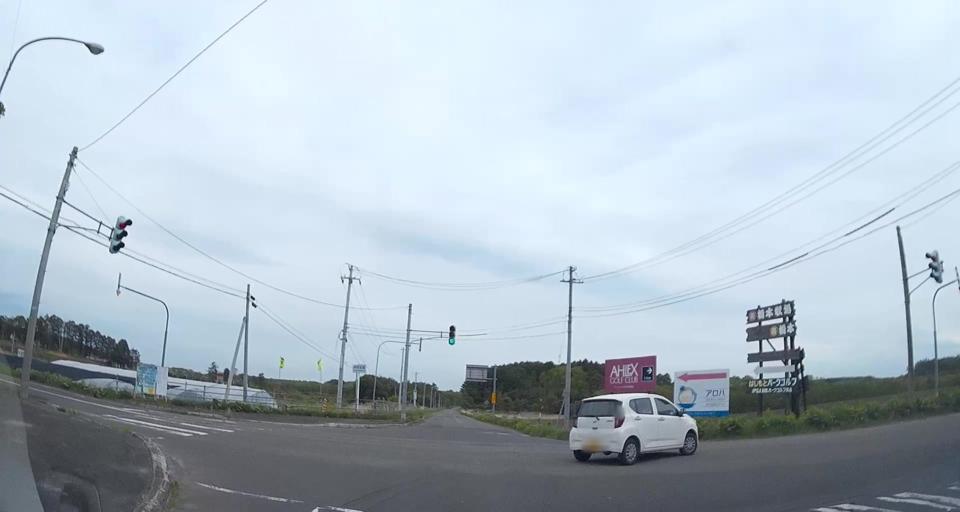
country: JP
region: Hokkaido
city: Chitose
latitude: 42.7743
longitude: 141.8339
